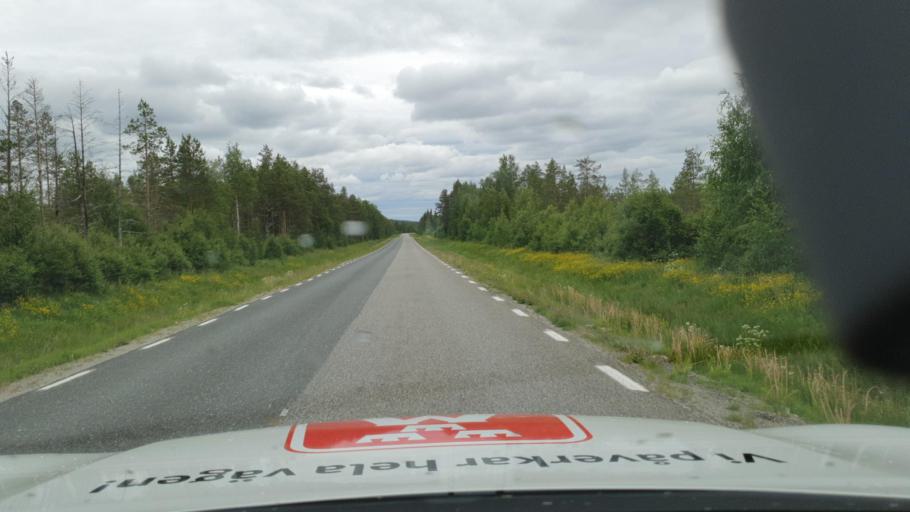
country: SE
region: Vaesterbotten
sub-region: Lycksele Kommun
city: Soderfors
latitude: 64.2787
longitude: 18.1955
